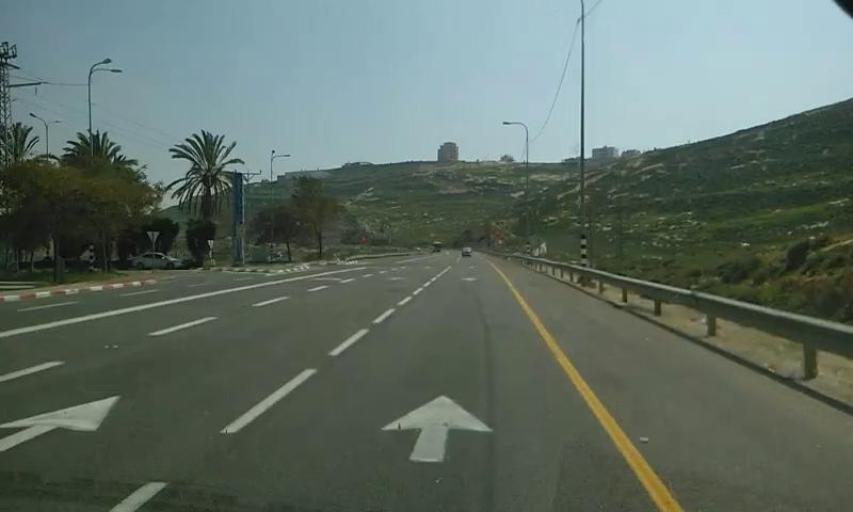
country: PS
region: West Bank
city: Jaba`
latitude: 31.8643
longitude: 35.2594
